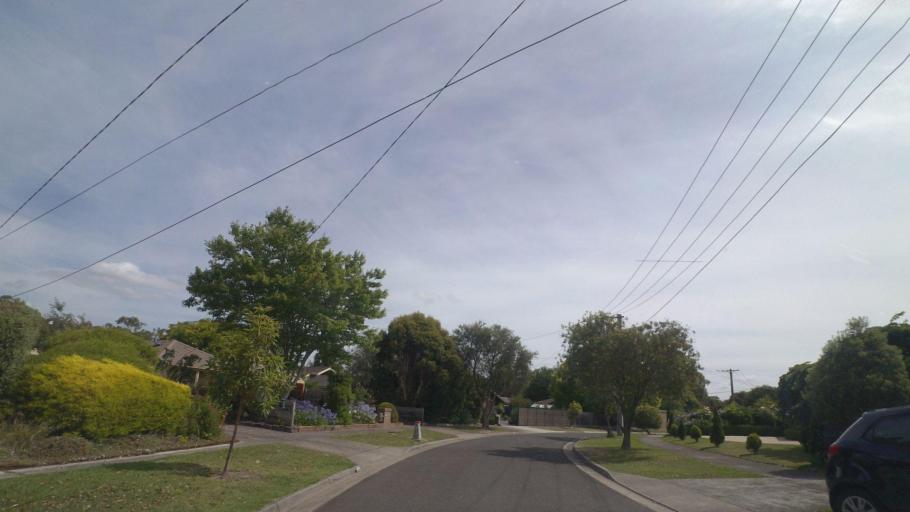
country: AU
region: Victoria
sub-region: Knox
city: The Basin
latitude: -37.8428
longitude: 145.3053
